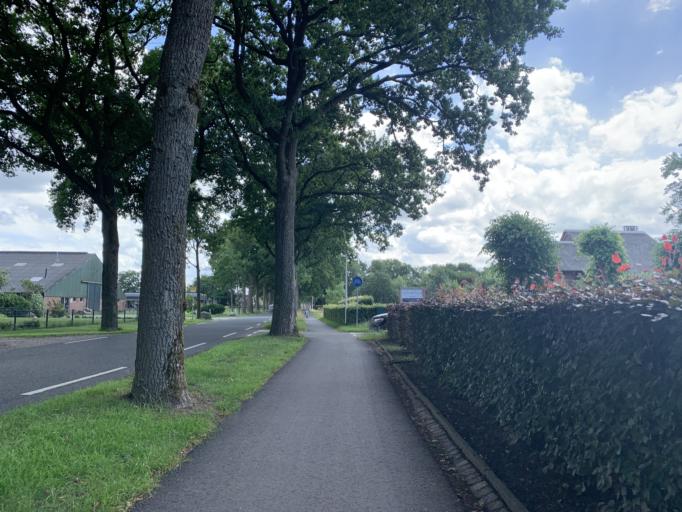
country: NL
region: Groningen
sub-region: Gemeente Haren
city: Haren
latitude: 53.1423
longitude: 6.6508
